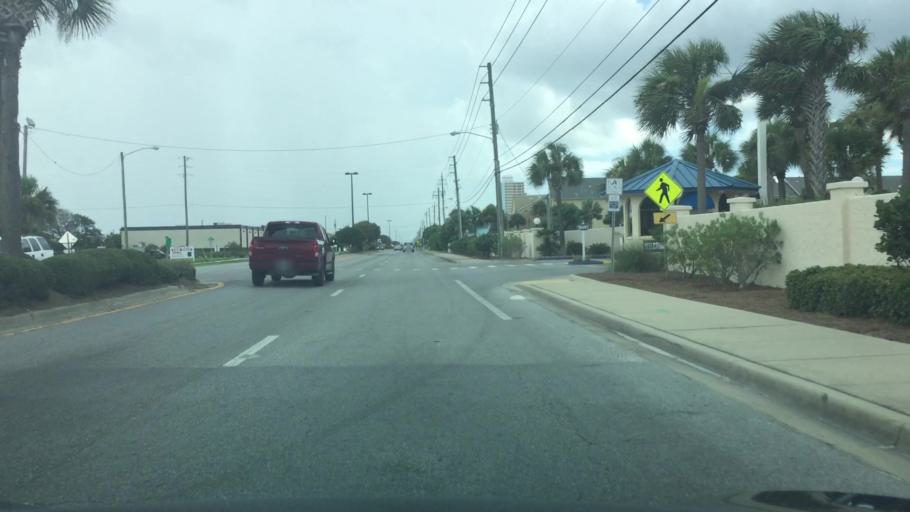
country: US
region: Florida
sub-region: Bay County
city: Lower Grand Lagoon
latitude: 30.1476
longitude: -85.7609
